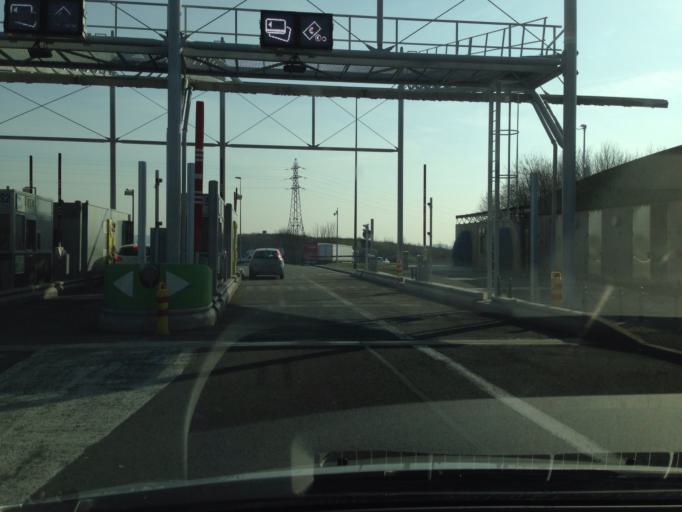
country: FR
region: Nord-Pas-de-Calais
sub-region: Departement du Pas-de-Calais
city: Saint-Josse
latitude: 50.5072
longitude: 1.6794
